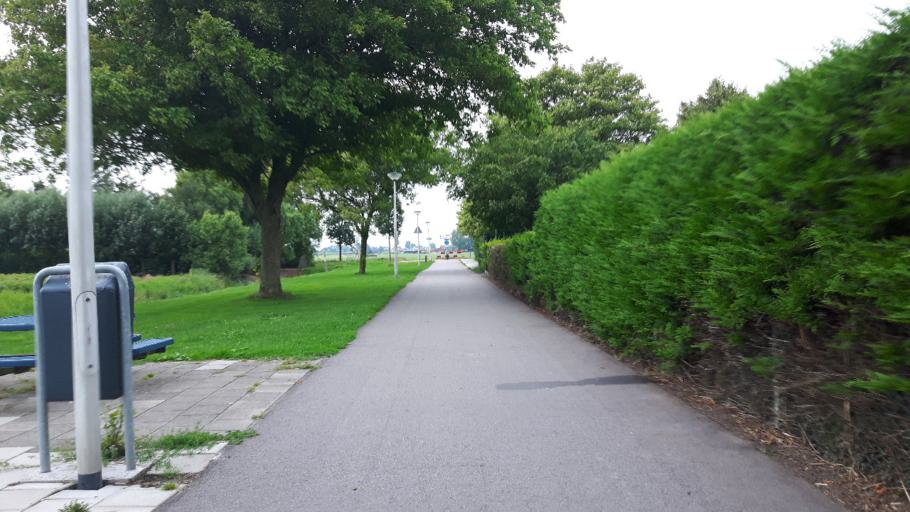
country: NL
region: South Holland
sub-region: Gemeente Nieuwkoop
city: Nieuwkoop
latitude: 52.1906
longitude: 4.7714
